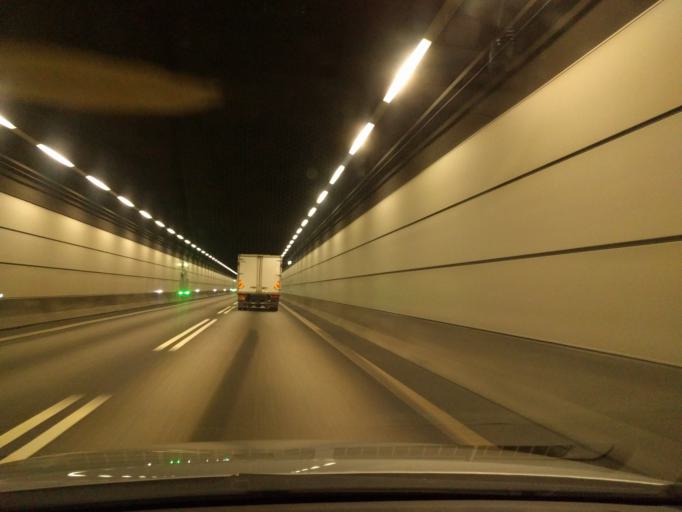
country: DK
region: Capital Region
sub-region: Dragor Kommune
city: Dragor
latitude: 55.6217
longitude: 12.7005
